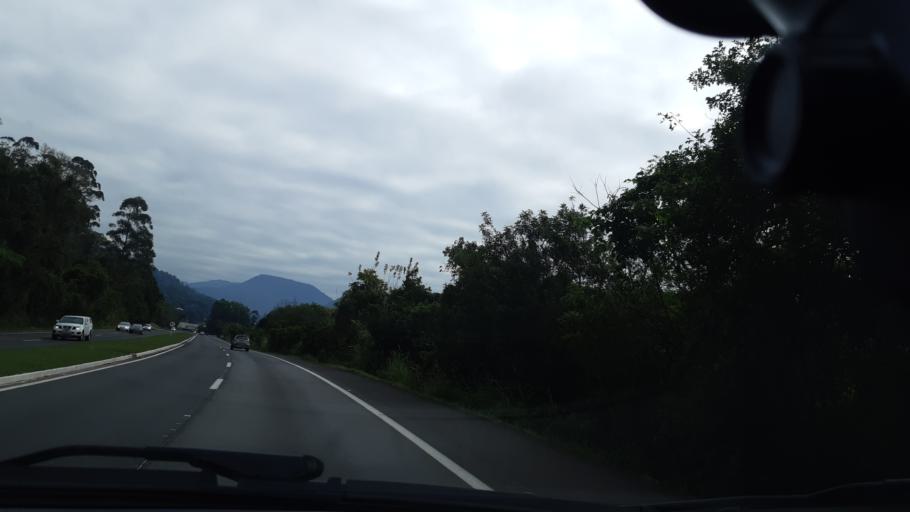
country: BR
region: Rio Grande do Sul
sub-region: Farroupilha
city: Farroupilha
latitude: -29.4063
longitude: -51.3529
